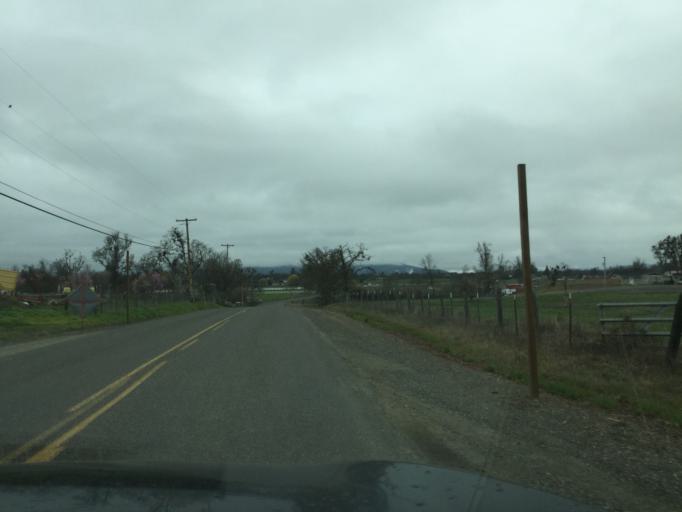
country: US
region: Oregon
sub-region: Jackson County
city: Central Point
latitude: 42.4007
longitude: -122.9093
